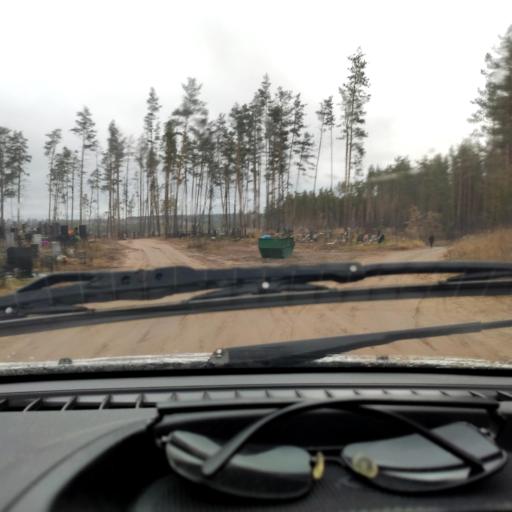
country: RU
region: Samara
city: Zhigulevsk
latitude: 53.5335
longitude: 49.5549
